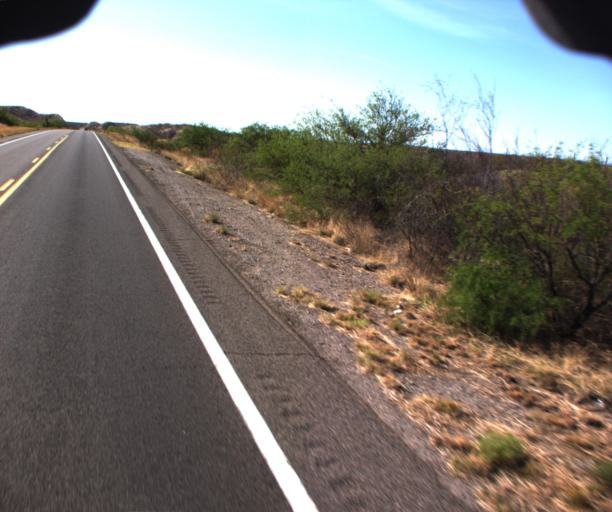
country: US
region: Arizona
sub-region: Cochise County
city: Saint David
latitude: 31.8307
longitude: -110.1811
